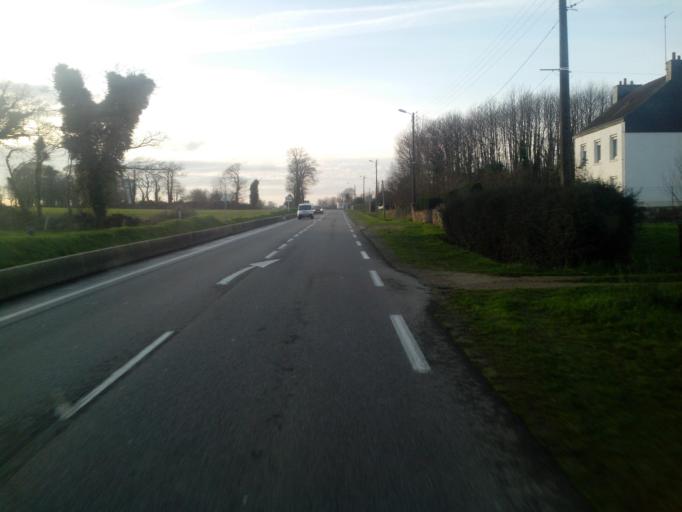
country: FR
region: Brittany
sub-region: Departement du Morbihan
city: Hennebont
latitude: 47.8161
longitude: -3.2366
